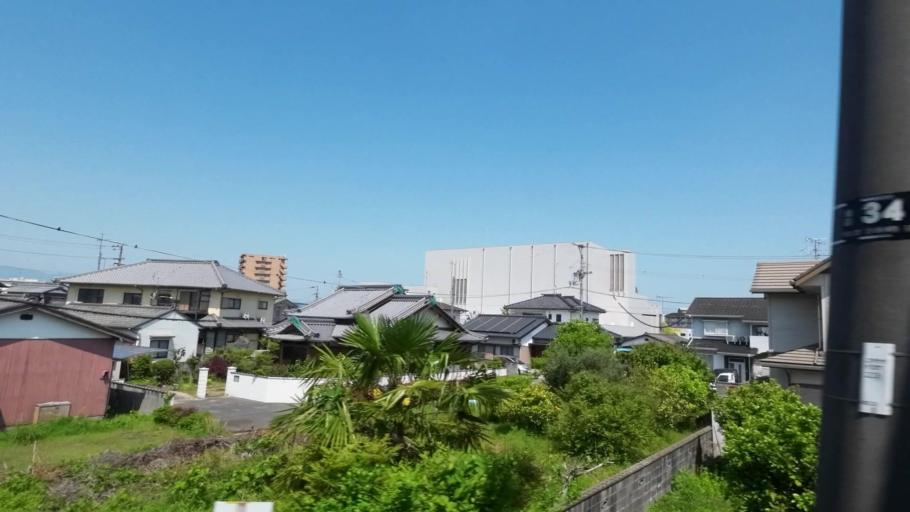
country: JP
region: Ehime
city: Saijo
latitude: 33.9103
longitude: 133.1833
